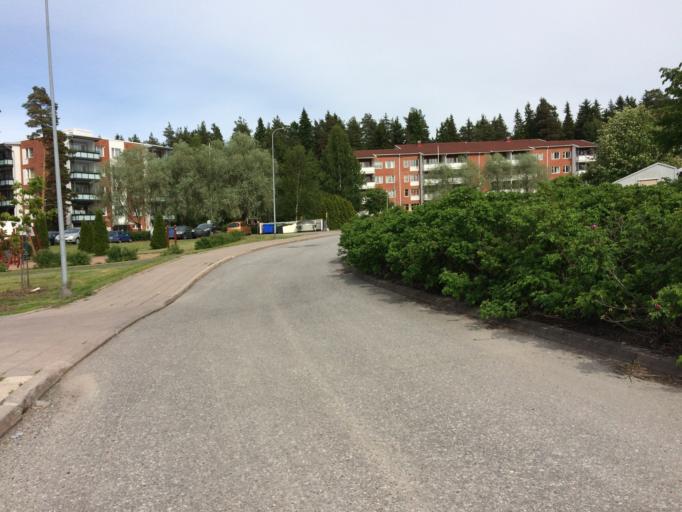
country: FI
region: Varsinais-Suomi
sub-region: Turku
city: Turku
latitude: 60.4735
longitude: 22.3209
